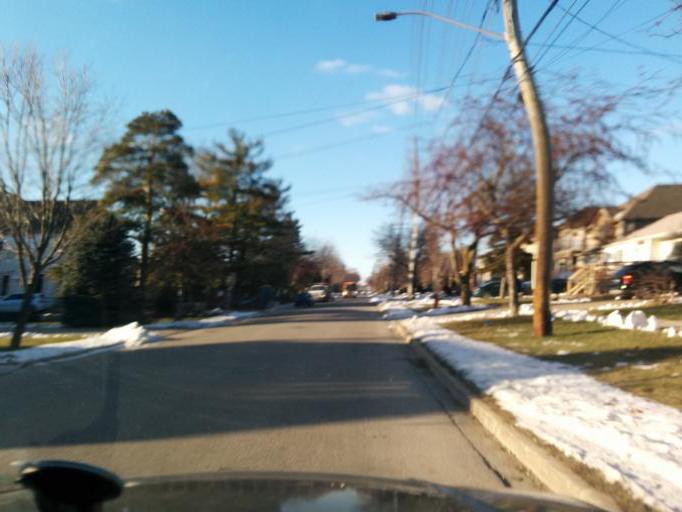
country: CA
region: Ontario
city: Mississauga
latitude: 43.5526
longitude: -79.6359
